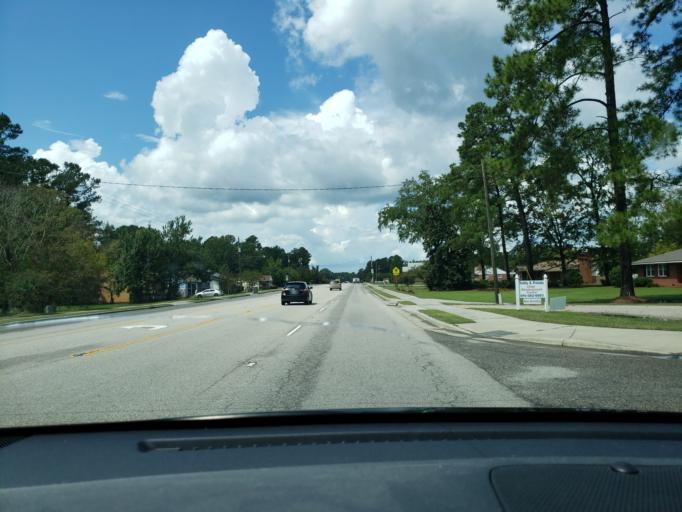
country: US
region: North Carolina
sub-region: Bladen County
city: Elizabethtown
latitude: 34.6529
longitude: -78.7169
